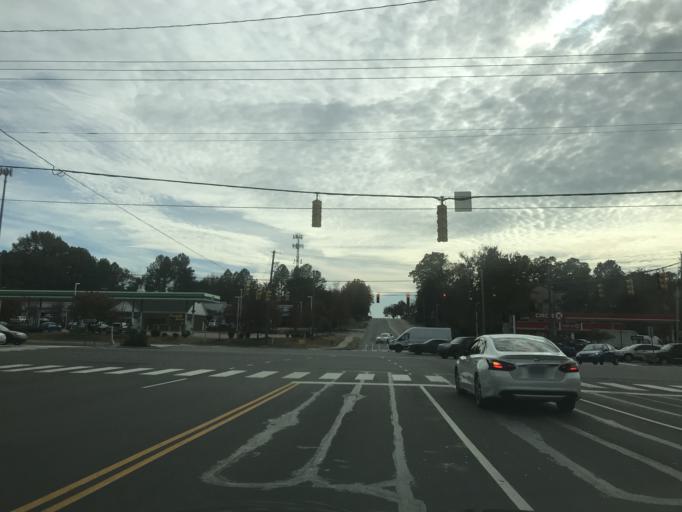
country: US
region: North Carolina
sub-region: Wake County
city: Raleigh
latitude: 35.7994
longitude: -78.5683
